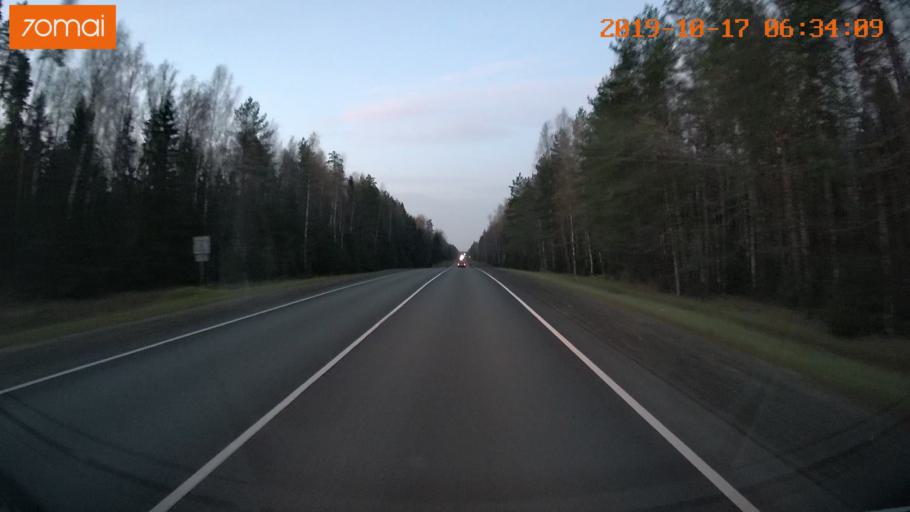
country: RU
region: Ivanovo
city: Novoye Leushino
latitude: 56.7064
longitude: 40.6436
